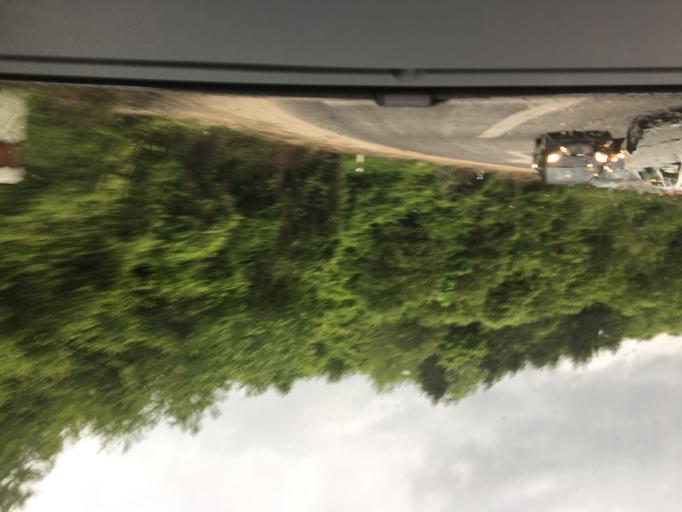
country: MK
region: Kicevo
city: Zajas
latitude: 41.6594
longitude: 20.8686
